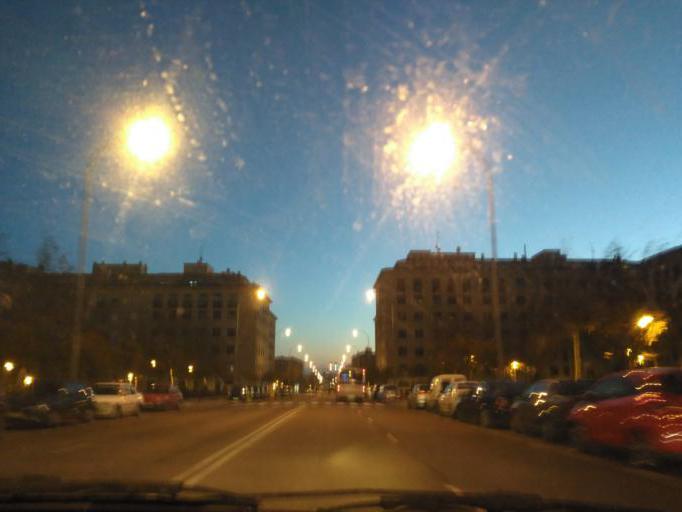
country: ES
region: Castille and Leon
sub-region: Provincia de Salamanca
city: Salamanca
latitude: 40.9823
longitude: -5.6672
